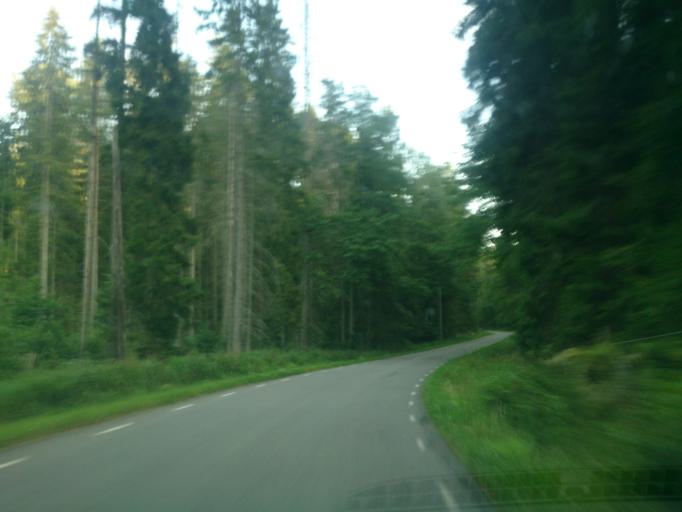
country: SE
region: OEstergoetland
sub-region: Atvidabergs Kommun
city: Atvidaberg
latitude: 58.2898
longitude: 16.0956
